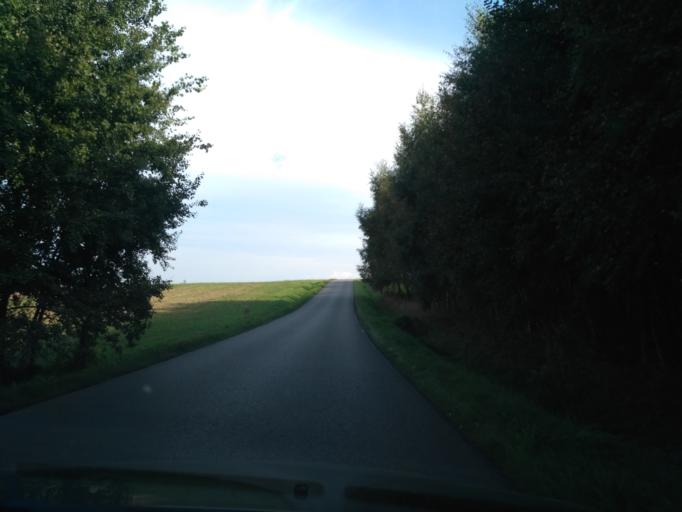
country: PL
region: Subcarpathian Voivodeship
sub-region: Powiat rzeszowski
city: Niechobrz
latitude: 50.0036
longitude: 21.8676
